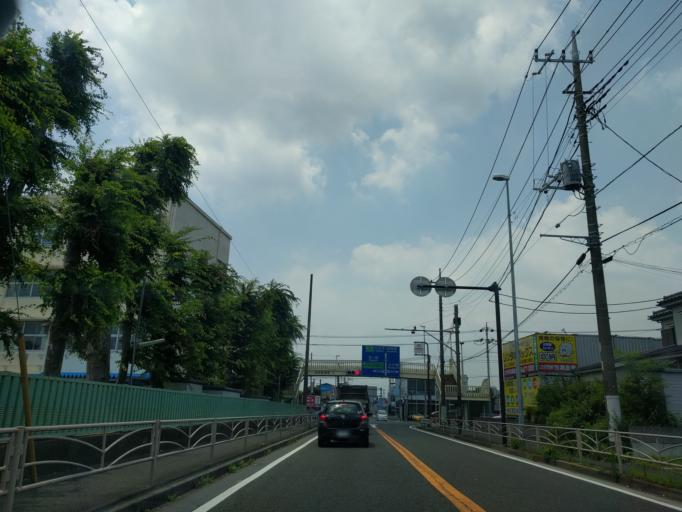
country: JP
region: Kanagawa
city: Minami-rinkan
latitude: 35.4856
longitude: 139.5219
